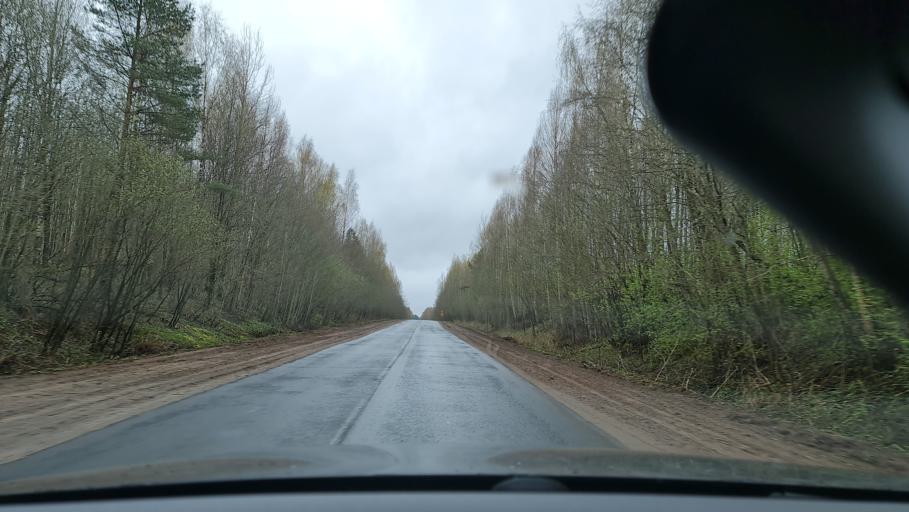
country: RU
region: Novgorod
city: Demyansk
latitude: 57.7400
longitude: 32.5733
